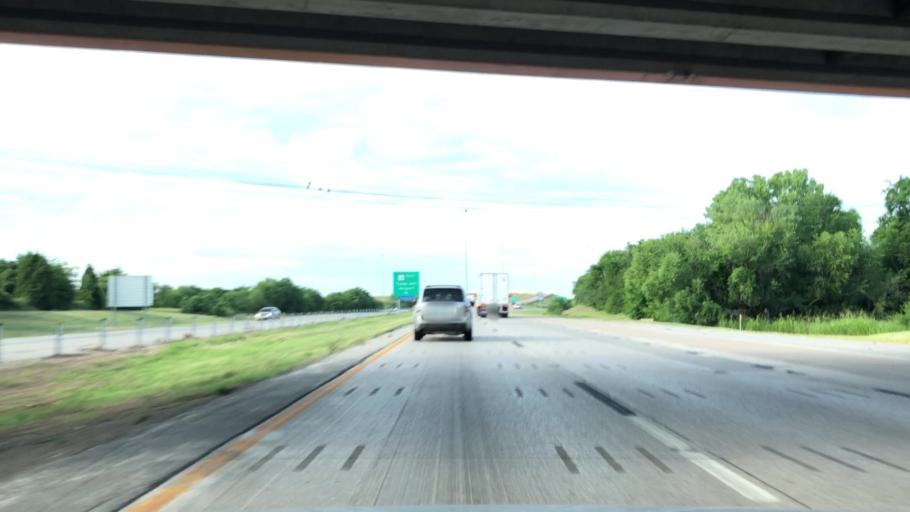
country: US
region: Oklahoma
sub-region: Tulsa County
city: Turley
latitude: 36.2061
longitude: -95.9469
